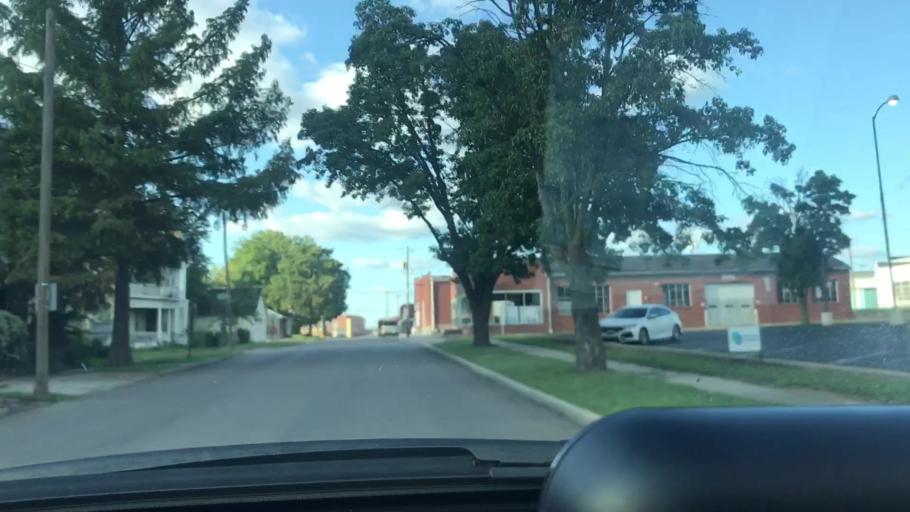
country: US
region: Missouri
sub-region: Pettis County
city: Sedalia
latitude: 38.7065
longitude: -93.2303
